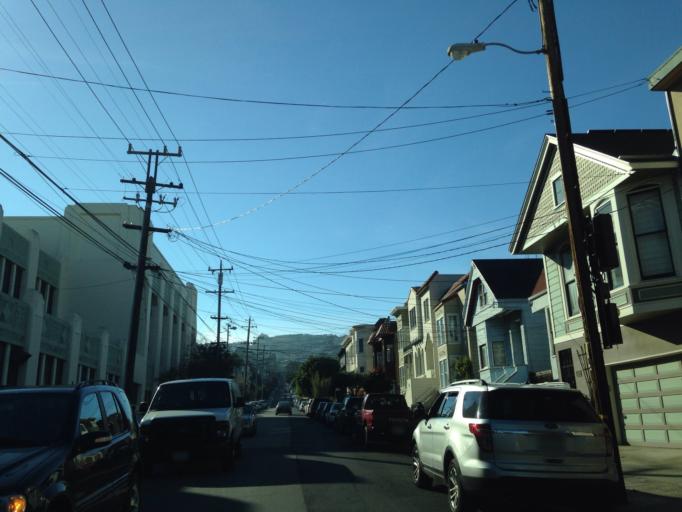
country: US
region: California
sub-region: San Francisco County
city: San Francisco
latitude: 37.7498
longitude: -122.4320
